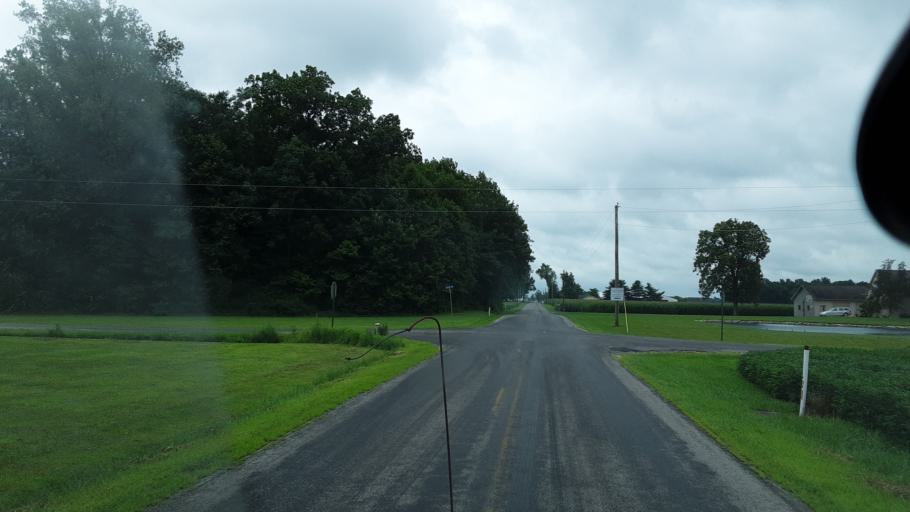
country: US
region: Indiana
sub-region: Wells County
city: Ossian
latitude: 40.8597
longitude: -85.1093
